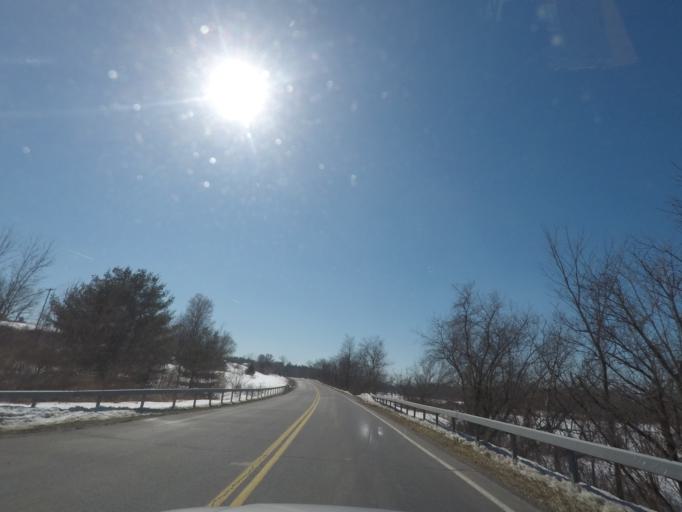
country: US
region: New York
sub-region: Saratoga County
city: Stillwater
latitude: 42.9906
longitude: -73.6029
